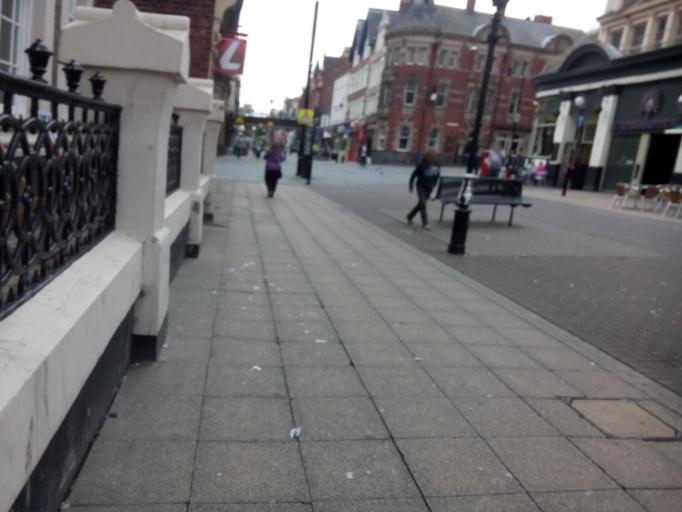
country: GB
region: England
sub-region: South Tyneside
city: South Shields
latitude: 54.9992
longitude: -1.4308
